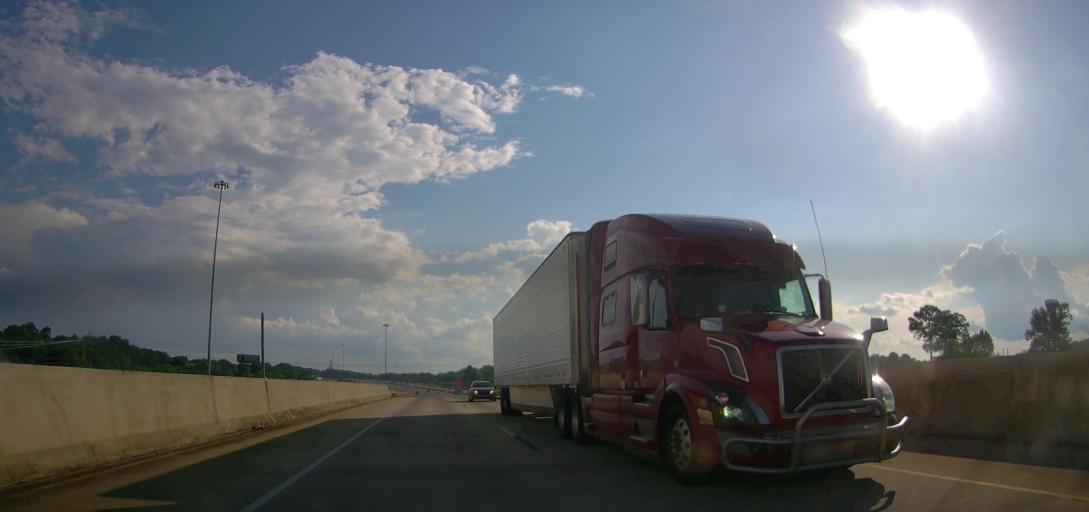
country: US
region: Alabama
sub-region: Jefferson County
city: Fultondale
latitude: 33.5698
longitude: -86.8188
